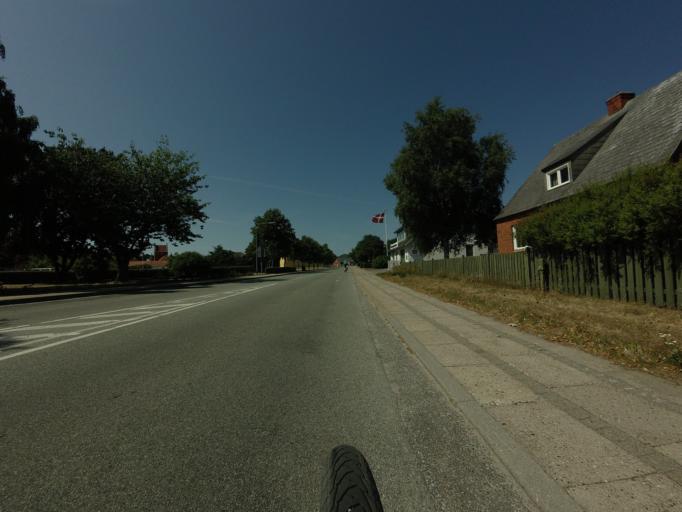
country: DK
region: North Denmark
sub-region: Laeso Kommune
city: Byrum
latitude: 57.2542
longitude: 11.0023
